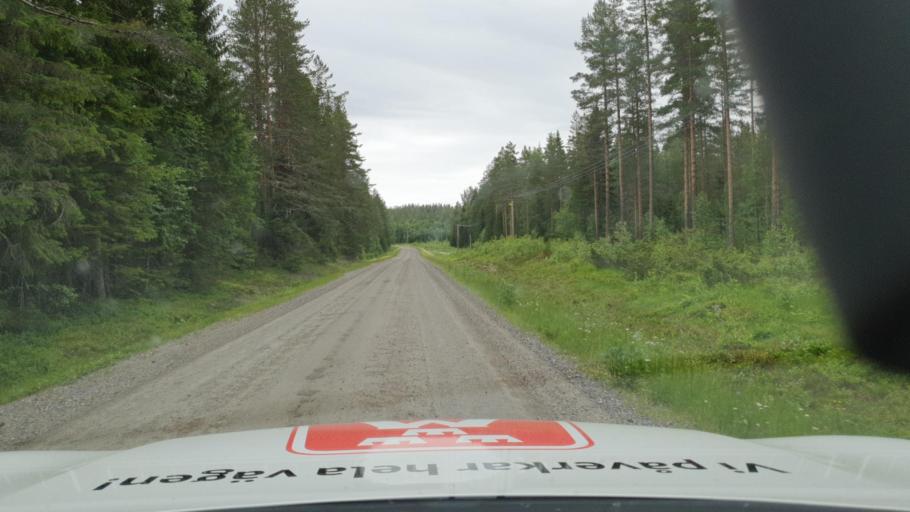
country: SE
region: Vaesterbotten
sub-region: Nordmalings Kommun
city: Nordmaling
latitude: 63.7344
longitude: 19.5032
